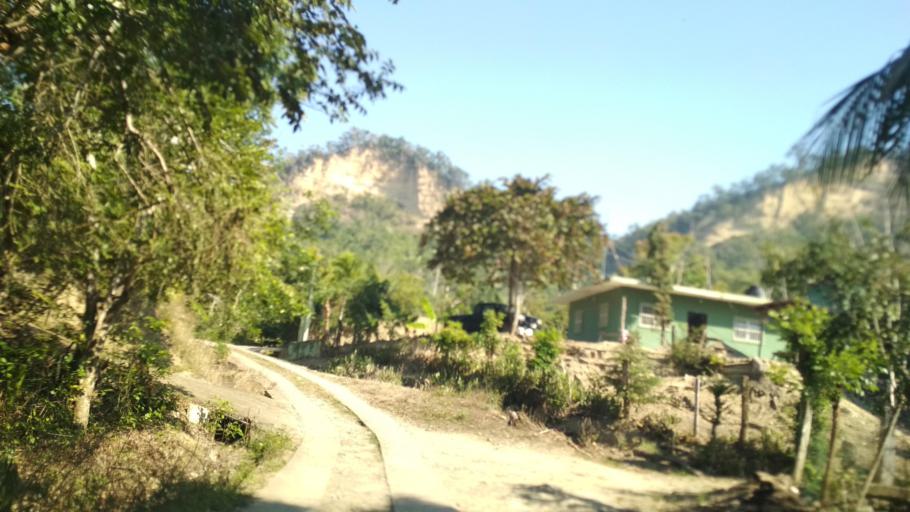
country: MX
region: Veracruz
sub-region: Papantla
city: Polutla
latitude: 20.4635
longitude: -97.1926
